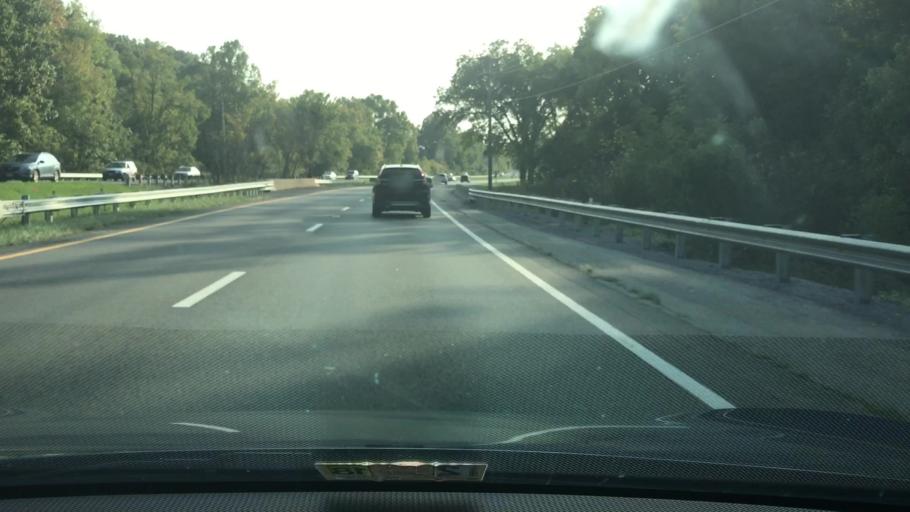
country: US
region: Virginia
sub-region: Botetourt County
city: Laymantown
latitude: 37.3404
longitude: -79.8513
